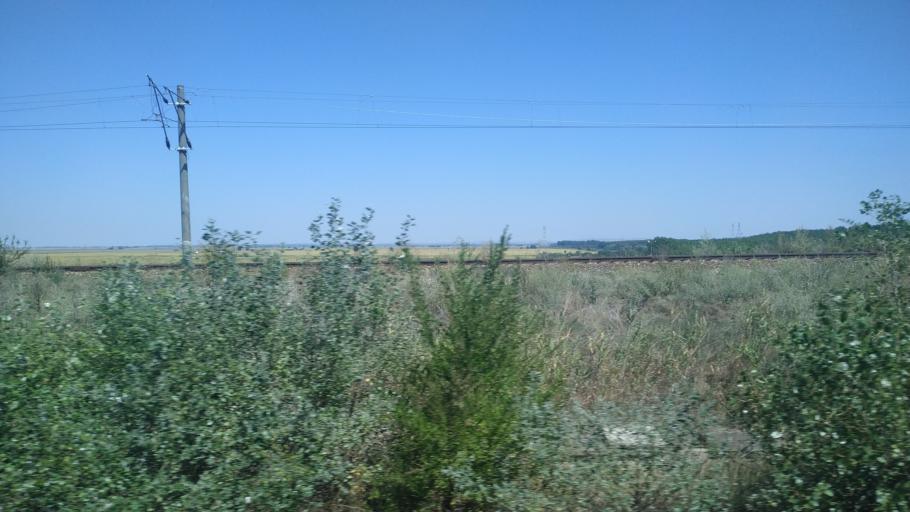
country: RO
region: Constanta
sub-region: Oras Cernavoda
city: Cernavoda
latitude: 44.3444
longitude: 27.9998
